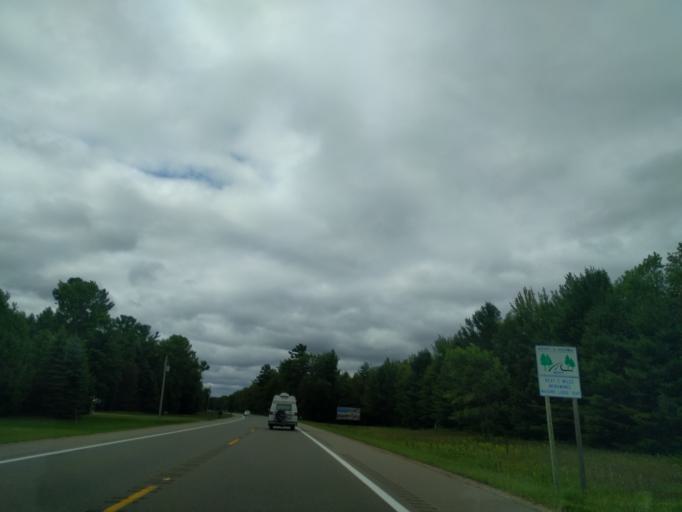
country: US
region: Michigan
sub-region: Menominee County
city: Menominee
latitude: 45.2786
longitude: -87.4610
